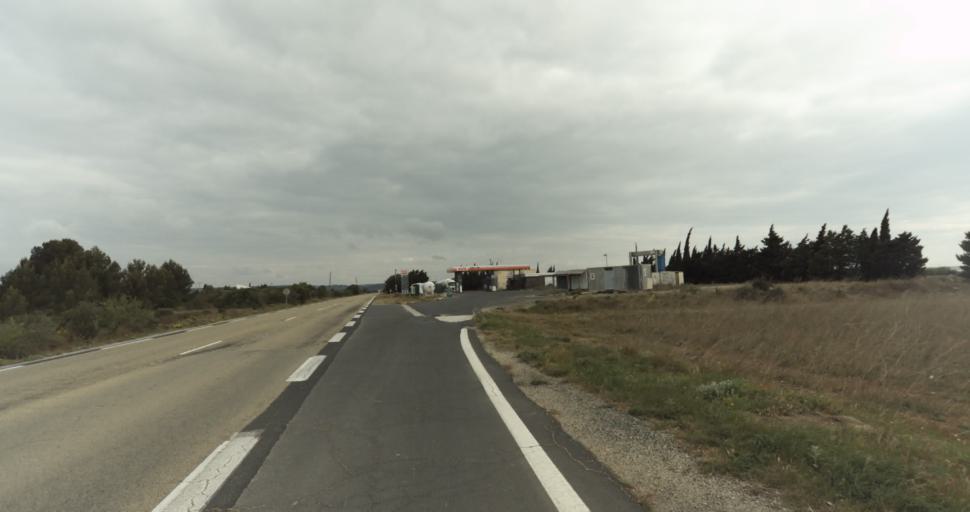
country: FR
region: Languedoc-Roussillon
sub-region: Departement de l'Aude
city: Leucate
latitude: 42.9444
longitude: 2.9890
